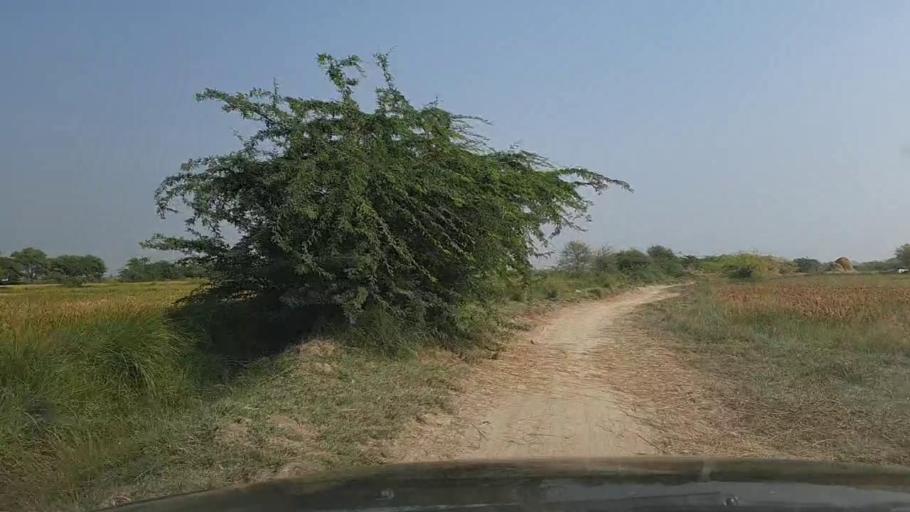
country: PK
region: Sindh
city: Mirpur Batoro
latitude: 24.6792
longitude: 68.2407
